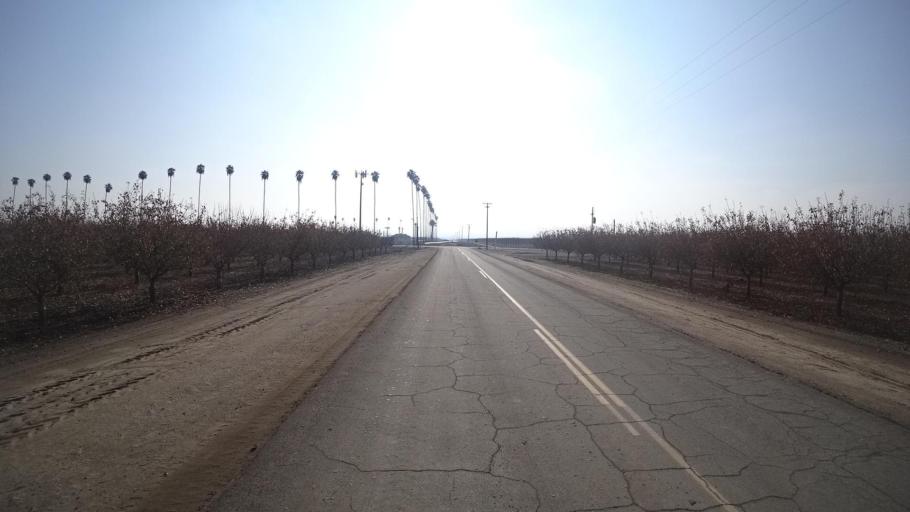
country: US
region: California
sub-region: Kern County
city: Buttonwillow
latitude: 35.3411
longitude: -119.3944
